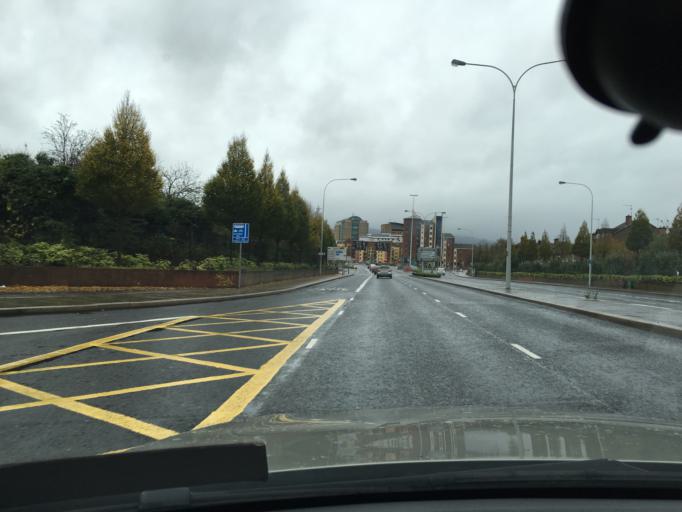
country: GB
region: Northern Ireland
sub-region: City of Belfast
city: Belfast
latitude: 54.5953
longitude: -5.9071
